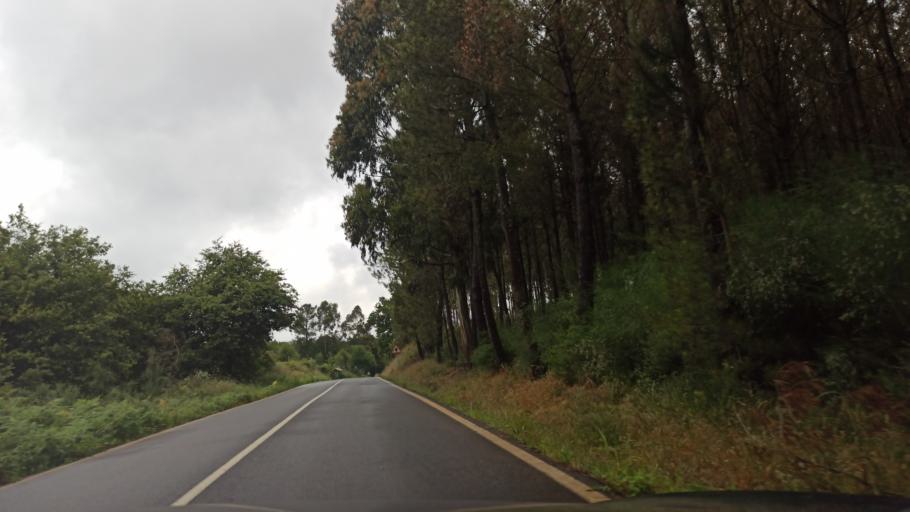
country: ES
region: Galicia
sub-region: Provincia da Coruna
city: Santiso
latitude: 42.7777
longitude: -8.0364
